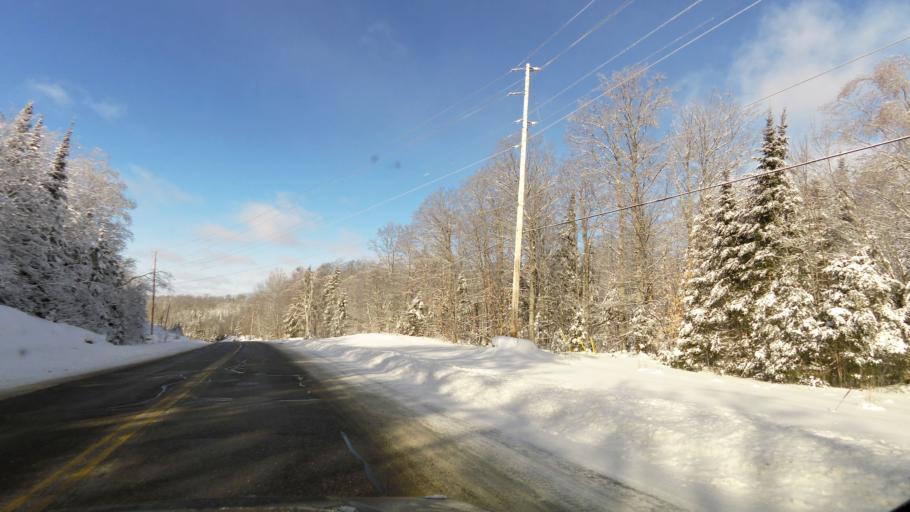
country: CA
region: Ontario
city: Bancroft
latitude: 45.0083
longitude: -78.3098
